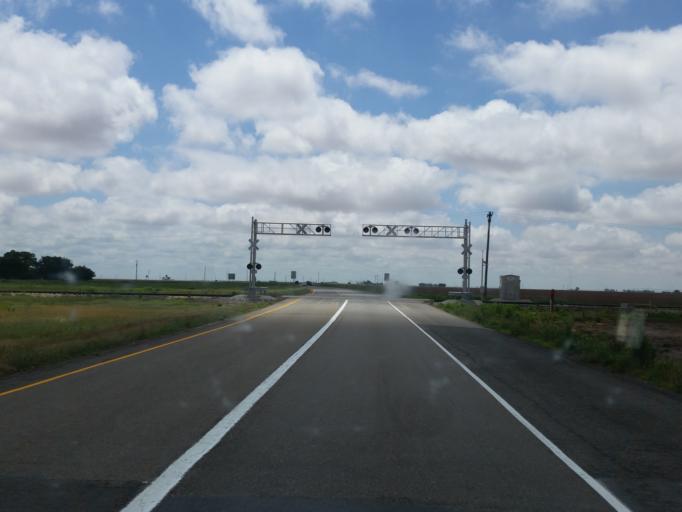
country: US
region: Texas
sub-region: Lubbock County
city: Slaton
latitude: 33.4152
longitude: -101.6354
